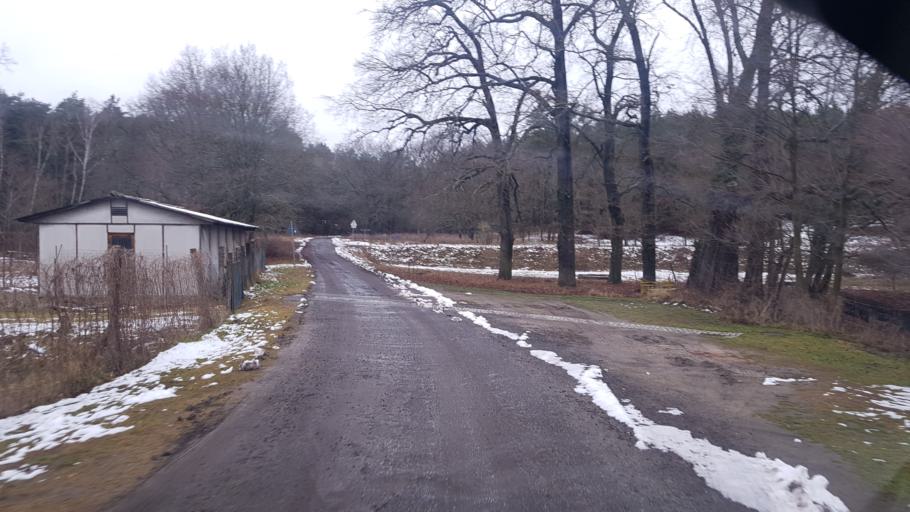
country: DE
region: Brandenburg
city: Jamlitz
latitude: 51.9934
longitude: 14.3528
